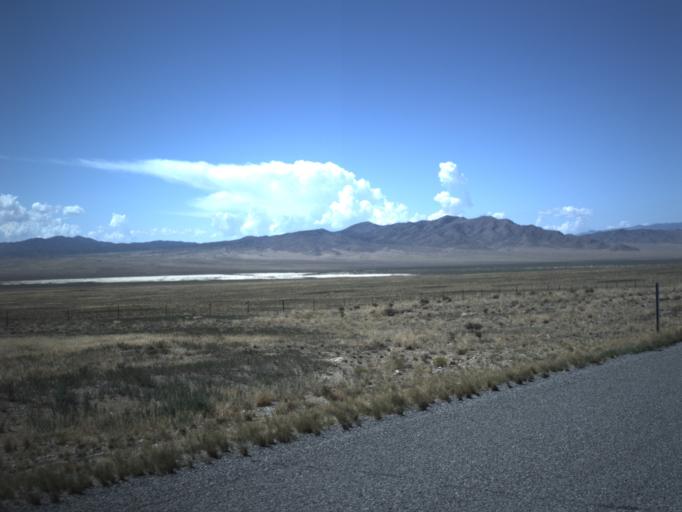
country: US
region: Utah
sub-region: Beaver County
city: Milford
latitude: 39.0417
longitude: -113.8090
